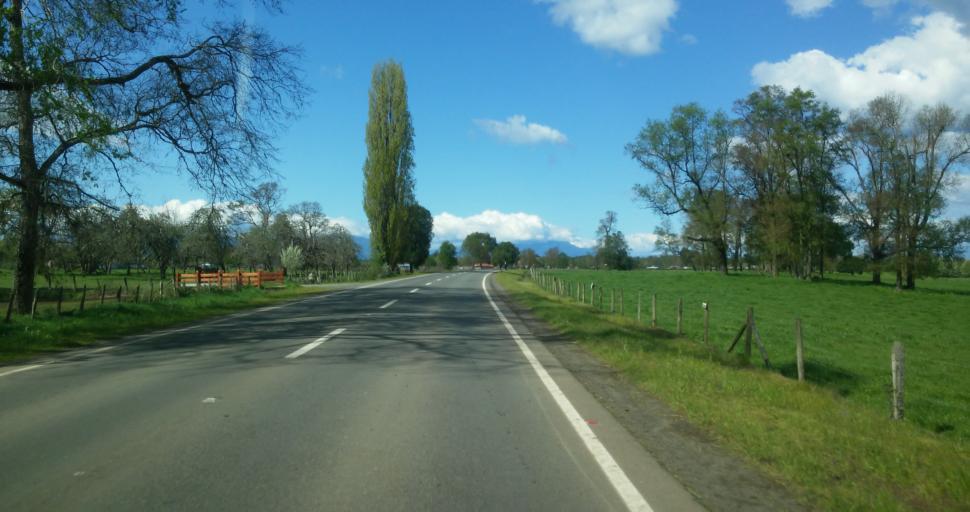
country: CL
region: Los Rios
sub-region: Provincia del Ranco
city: Rio Bueno
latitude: -40.2409
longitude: -72.6061
